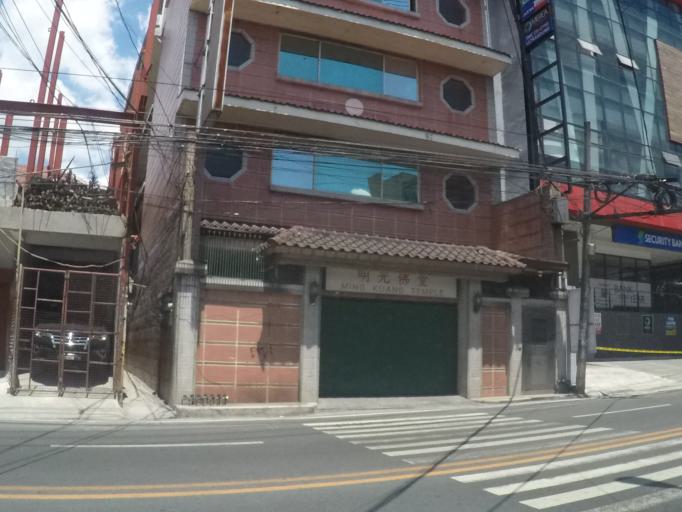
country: PH
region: Metro Manila
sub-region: San Juan
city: San Juan
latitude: 14.6014
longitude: 121.0275
